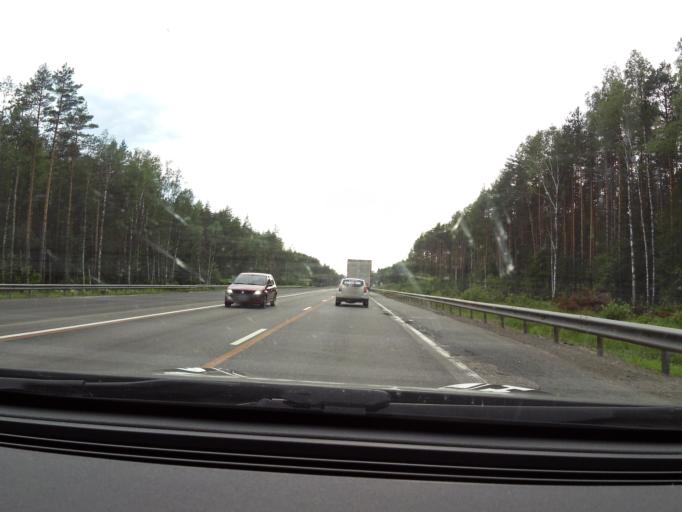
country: RU
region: Vladimir
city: Nikologory
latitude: 56.2355
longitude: 41.8924
